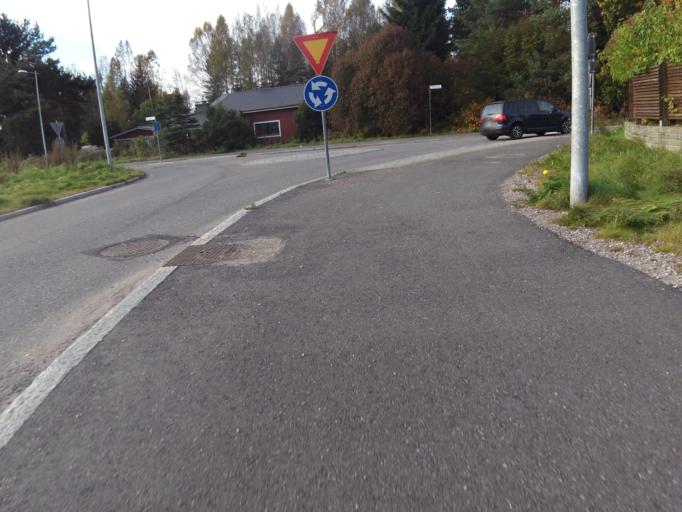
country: FI
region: Uusimaa
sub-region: Helsinki
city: Kauniainen
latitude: 60.2808
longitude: 24.7456
